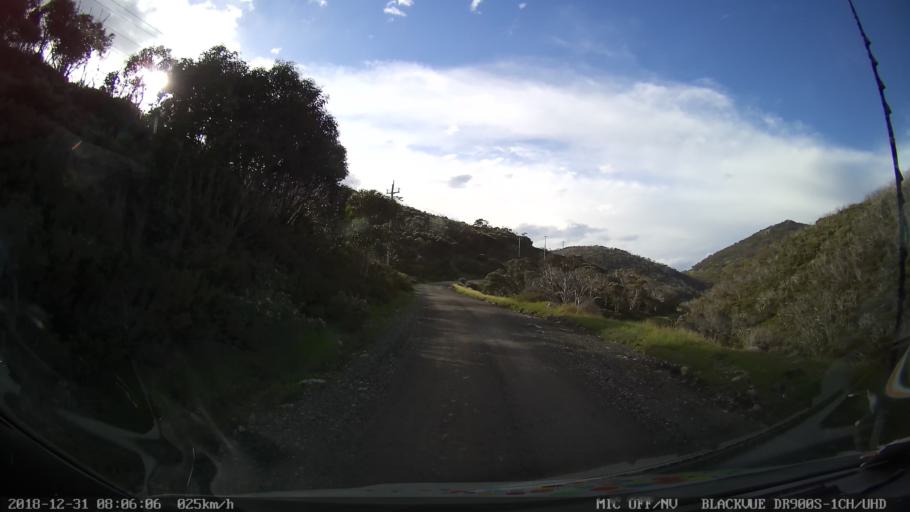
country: AU
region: New South Wales
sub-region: Snowy River
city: Jindabyne
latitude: -36.3735
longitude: 148.4076
